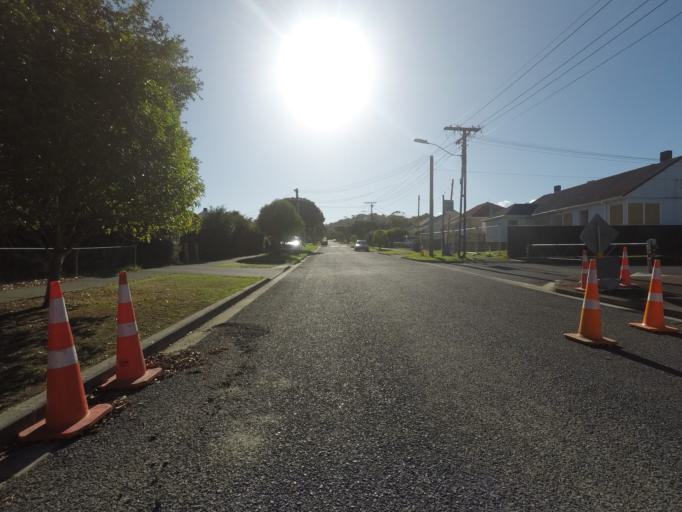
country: NZ
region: Auckland
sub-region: Auckland
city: Rosebank
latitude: -36.8956
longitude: 174.7126
